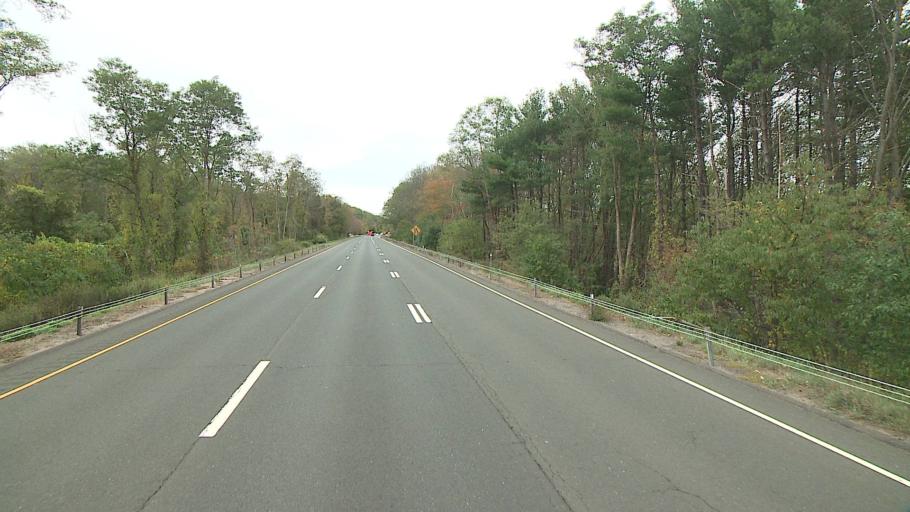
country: US
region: Connecticut
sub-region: Middlesex County
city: Higganum
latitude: 41.5067
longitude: -72.5881
